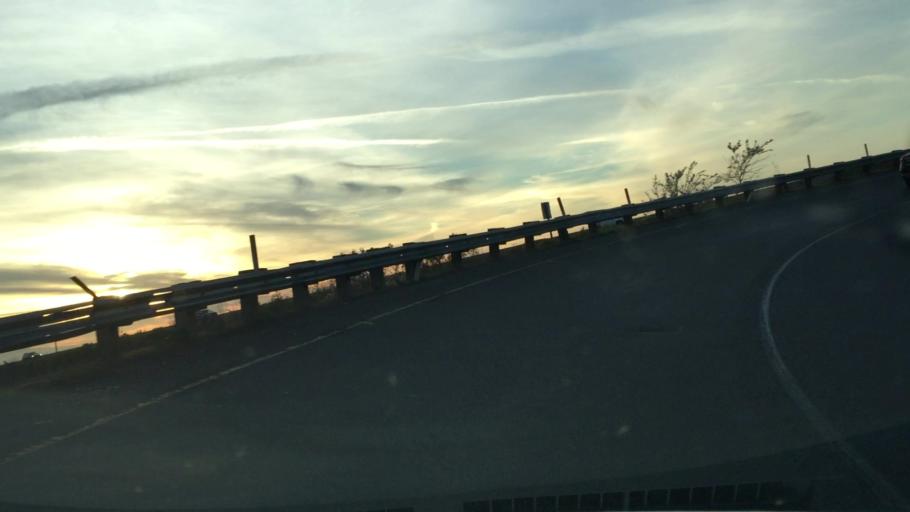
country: US
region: California
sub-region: Solano County
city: Vallejo
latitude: 38.1374
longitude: -122.2569
